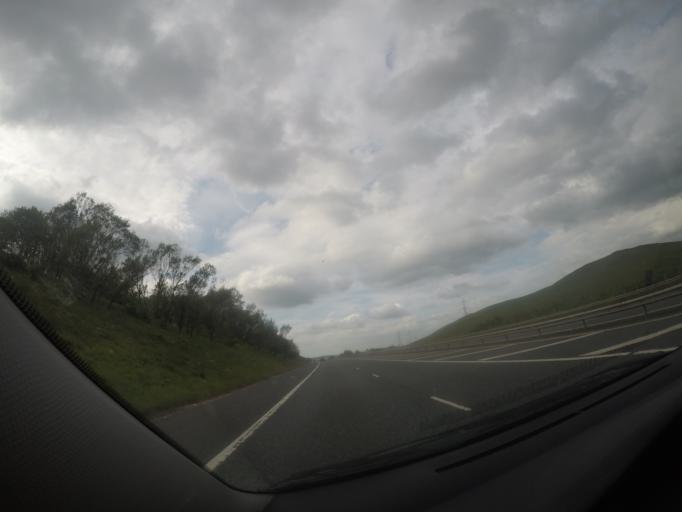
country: GB
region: Scotland
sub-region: South Lanarkshire
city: Douglas
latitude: 55.5562
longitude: -3.8018
